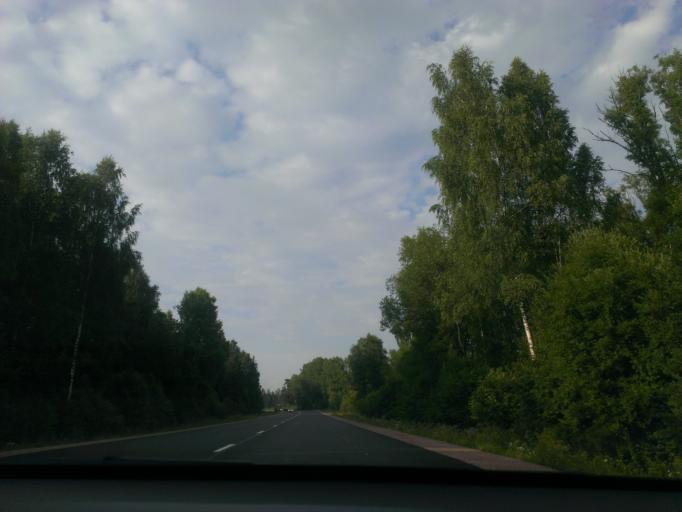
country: LV
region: Kekava
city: Kekava
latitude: 56.7178
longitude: 24.2501
